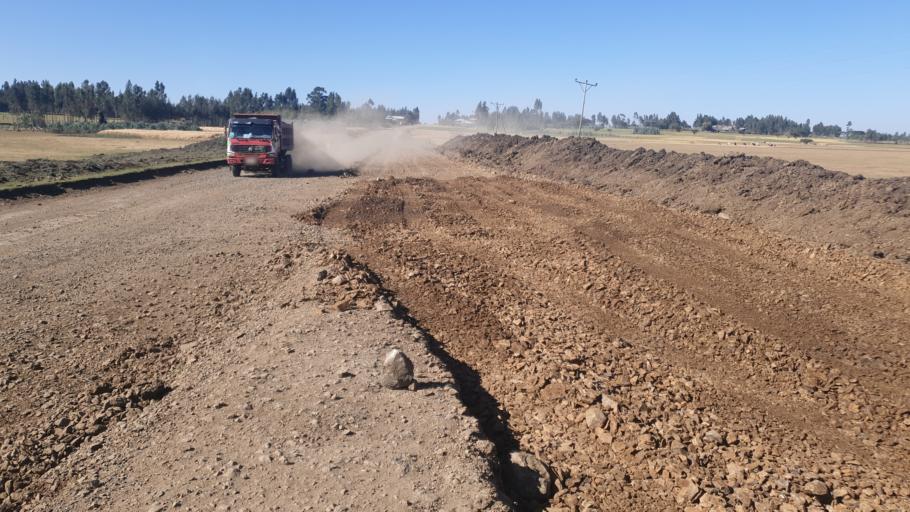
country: ET
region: Oromiya
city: Fiche
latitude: 9.5757
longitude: 38.9068
